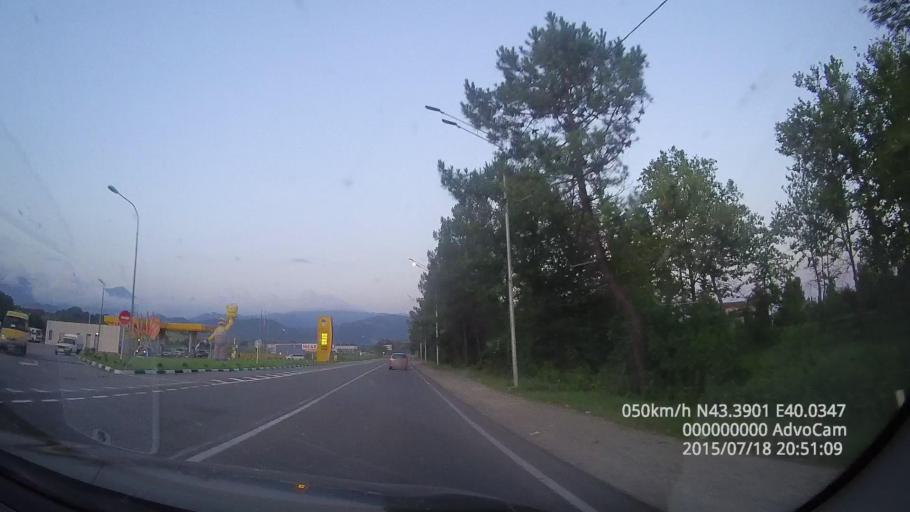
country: GE
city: Gantiadi
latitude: 43.3900
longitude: 40.0360
